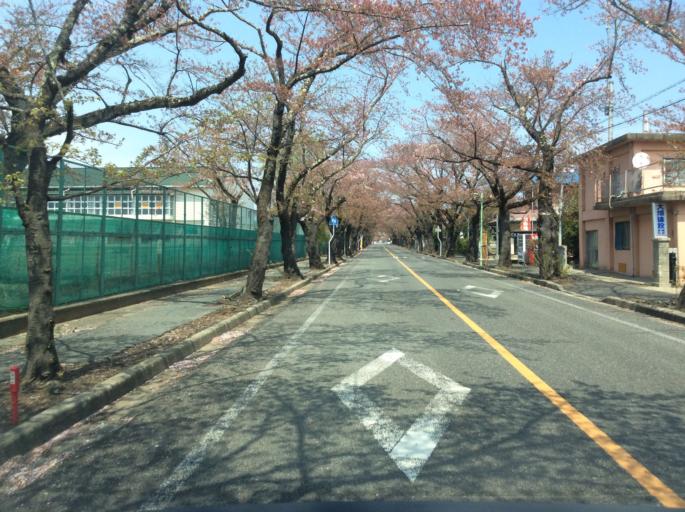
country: JP
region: Fukushima
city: Namie
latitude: 37.3586
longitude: 140.9959
